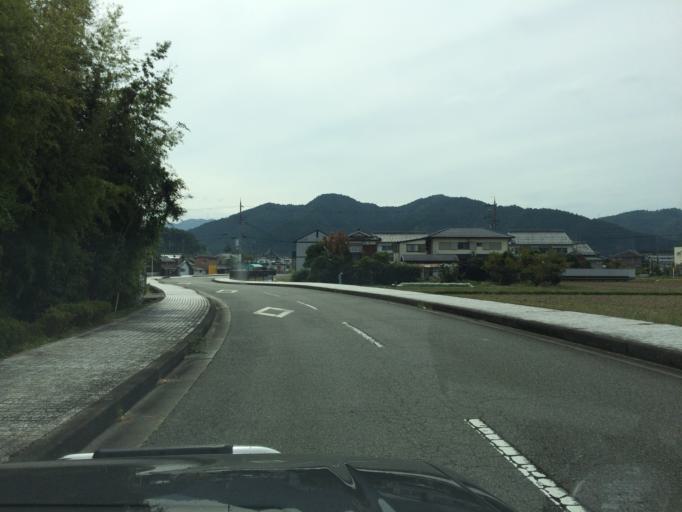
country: JP
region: Hyogo
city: Sasayama
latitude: 35.0717
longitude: 135.2135
